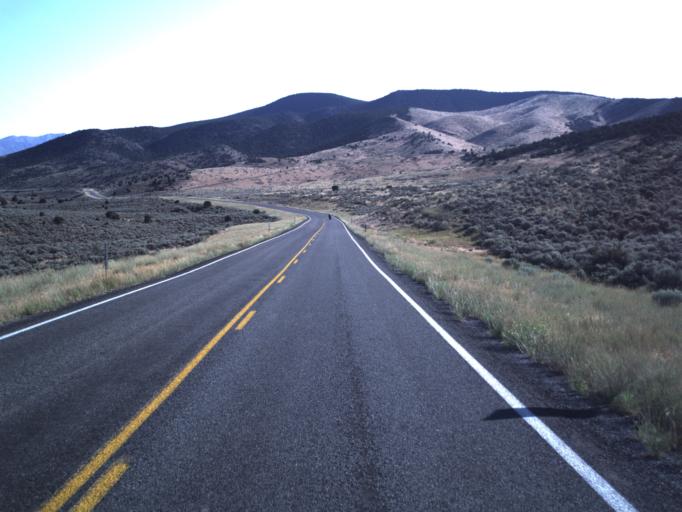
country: US
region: Utah
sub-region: Iron County
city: Parowan
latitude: 38.0892
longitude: -112.9531
